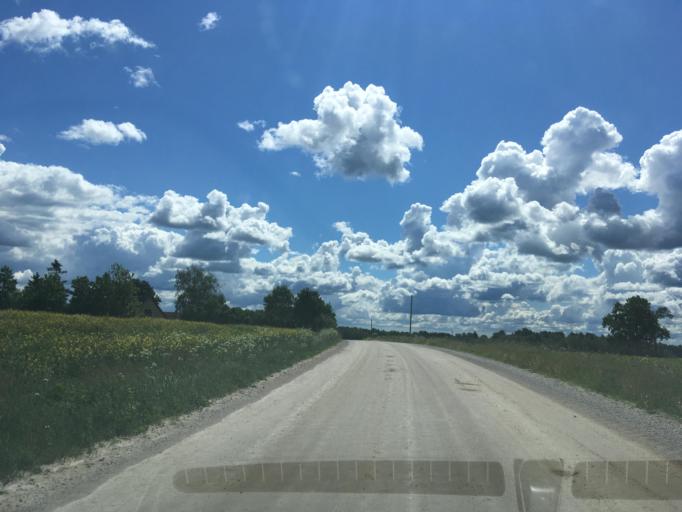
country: EE
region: Harju
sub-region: Nissi vald
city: Turba
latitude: 58.9275
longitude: 24.1535
